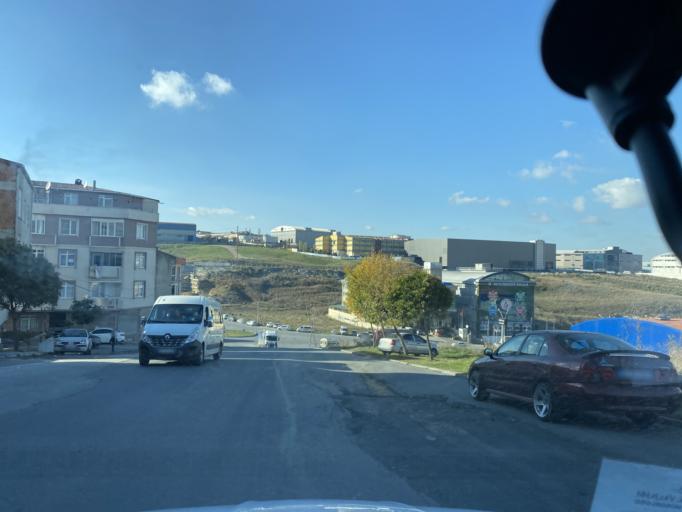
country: TR
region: Istanbul
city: Esenyurt
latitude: 41.0479
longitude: 28.6460
